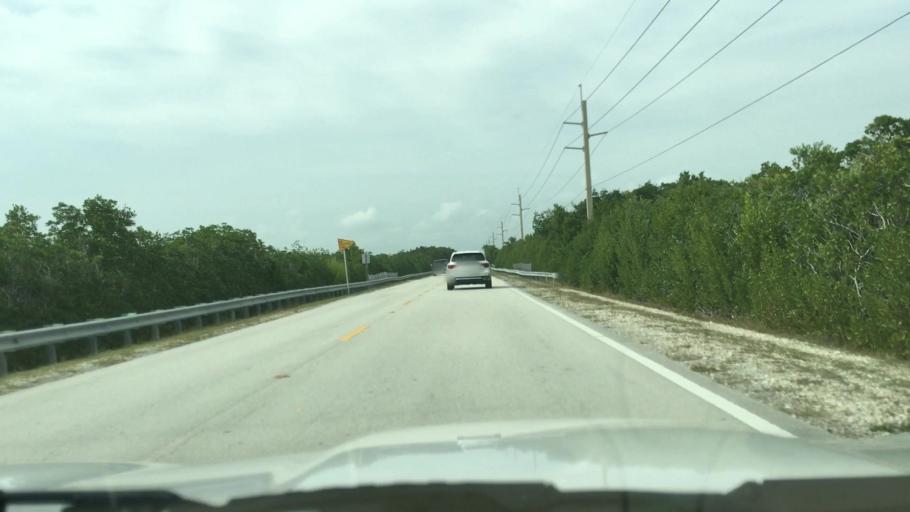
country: US
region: Florida
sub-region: Monroe County
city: North Key Largo
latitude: 25.2819
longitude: -80.3513
